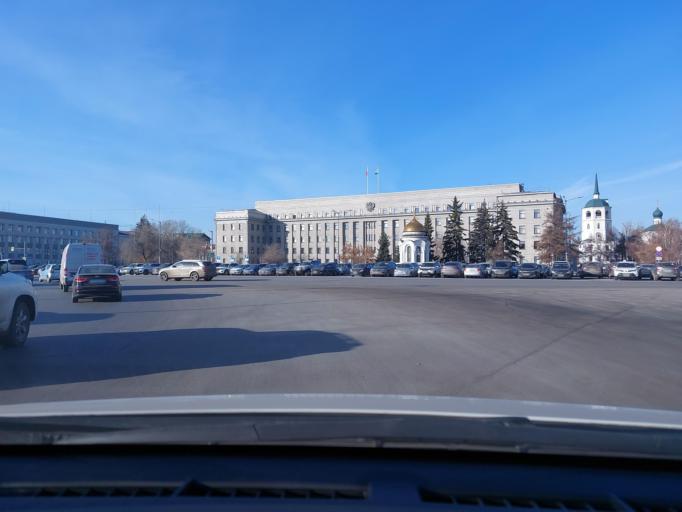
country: RU
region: Irkutsk
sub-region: Irkutskiy Rayon
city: Irkutsk
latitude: 52.2890
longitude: 104.2817
